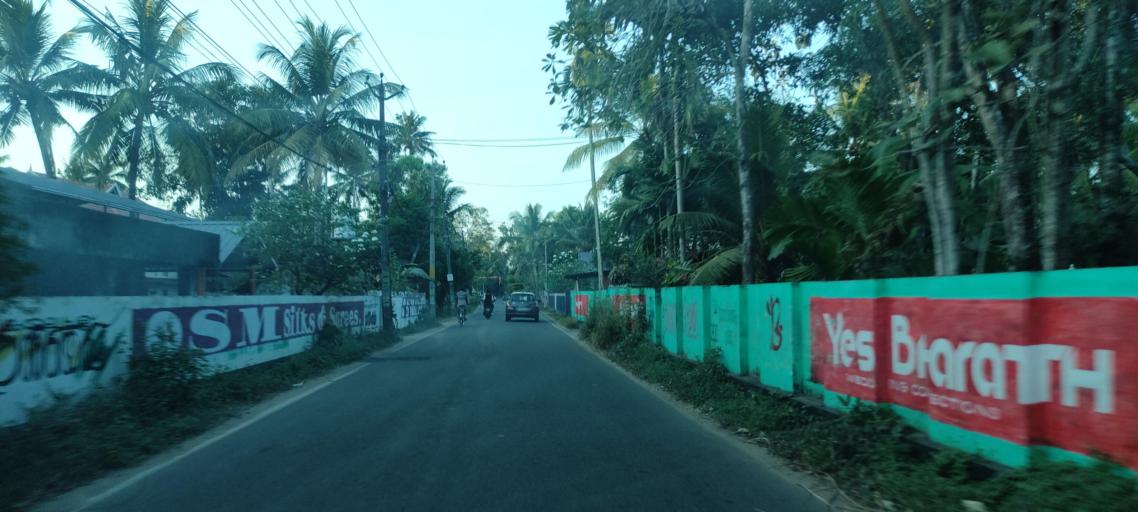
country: IN
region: Kerala
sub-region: Alappuzha
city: Kayankulam
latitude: 9.2472
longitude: 76.4523
